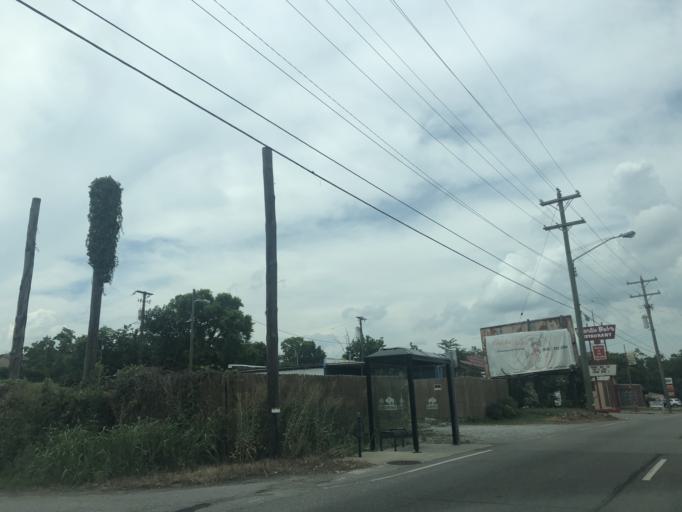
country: US
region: Tennessee
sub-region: Davidson County
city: Nashville
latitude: 36.1964
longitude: -86.7719
